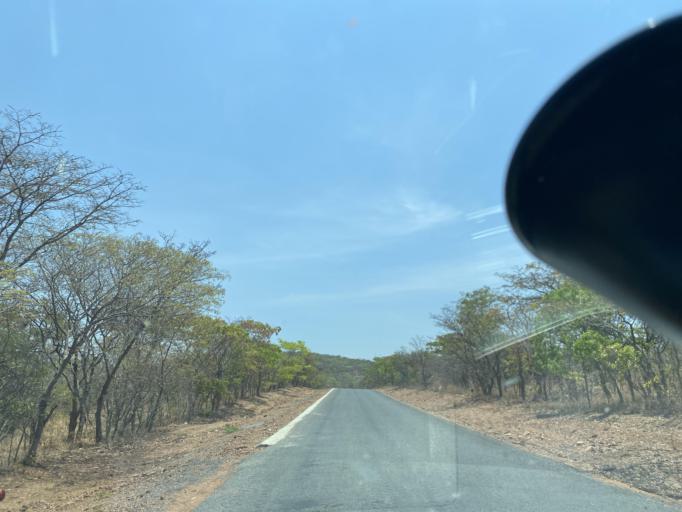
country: ZM
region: Lusaka
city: Kafue
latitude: -15.8637
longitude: 28.4271
